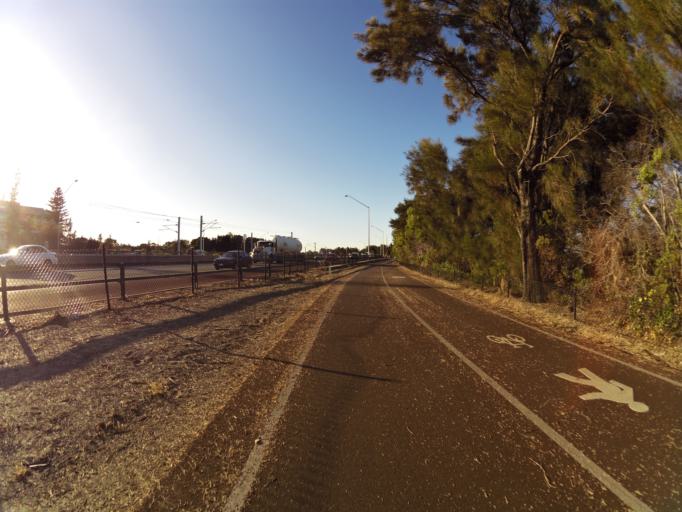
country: AU
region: Western Australia
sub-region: South Perth
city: South Perth
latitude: -31.9771
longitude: 115.8480
